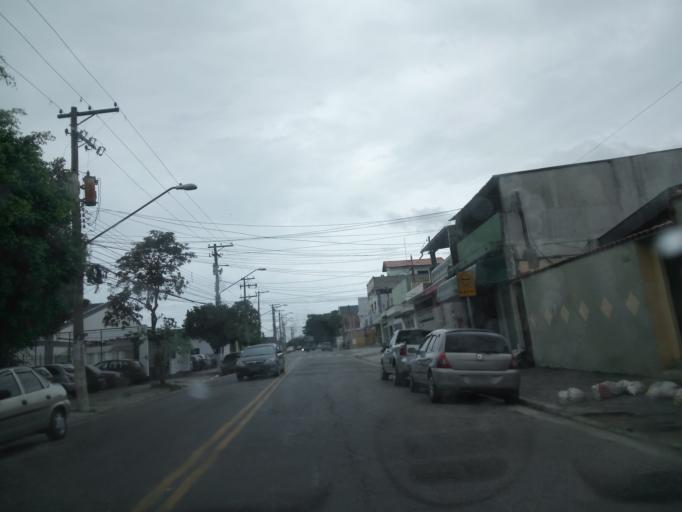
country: BR
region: Sao Paulo
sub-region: Sao Bernardo Do Campo
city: Sao Bernardo do Campo
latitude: -23.7038
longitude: -46.5798
